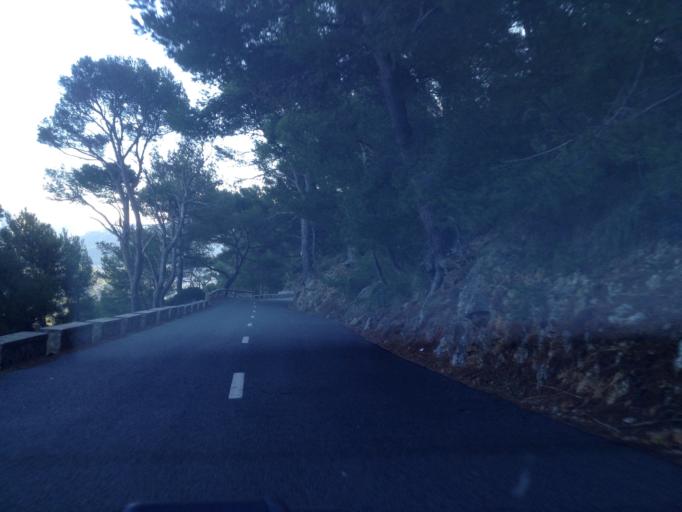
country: ES
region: Balearic Islands
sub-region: Illes Balears
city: Alcudia
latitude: 39.9303
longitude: 3.1230
